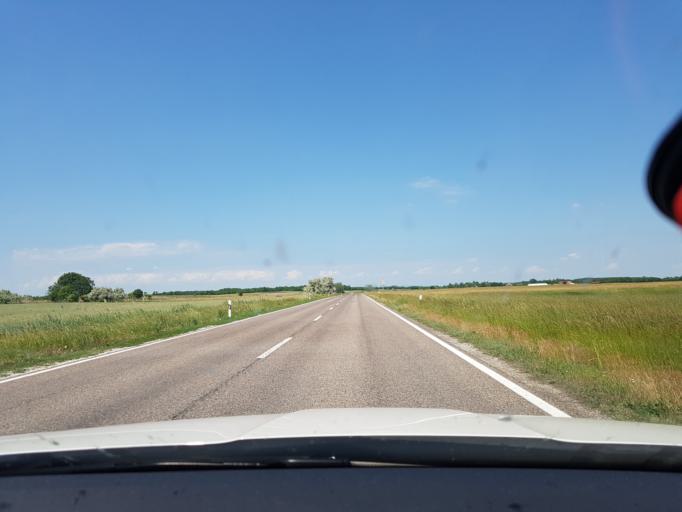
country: HU
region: Hajdu-Bihar
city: Egyek
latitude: 47.5774
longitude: 20.8559
